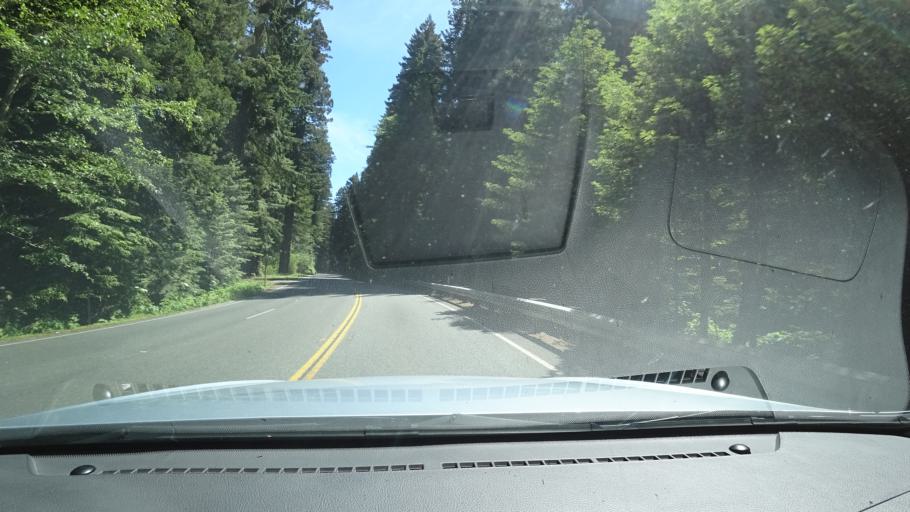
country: US
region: California
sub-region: Del Norte County
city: Bertsch-Oceanview
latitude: 41.6833
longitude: -124.1143
